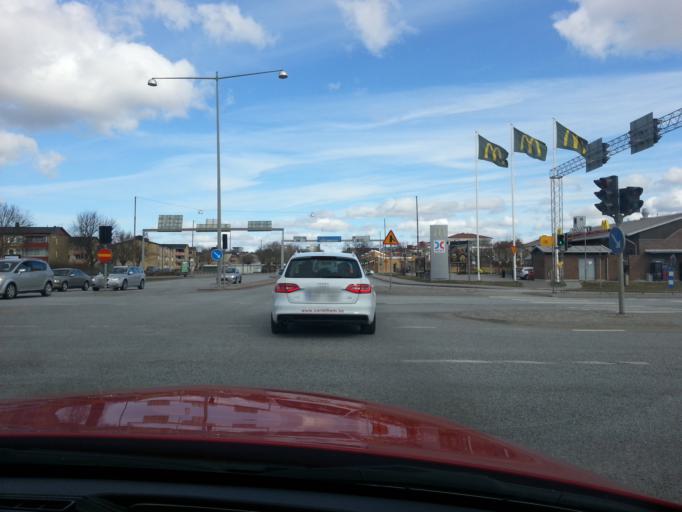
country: SE
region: Uppsala
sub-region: Uppsala Kommun
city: Uppsala
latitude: 59.8680
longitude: 17.6597
